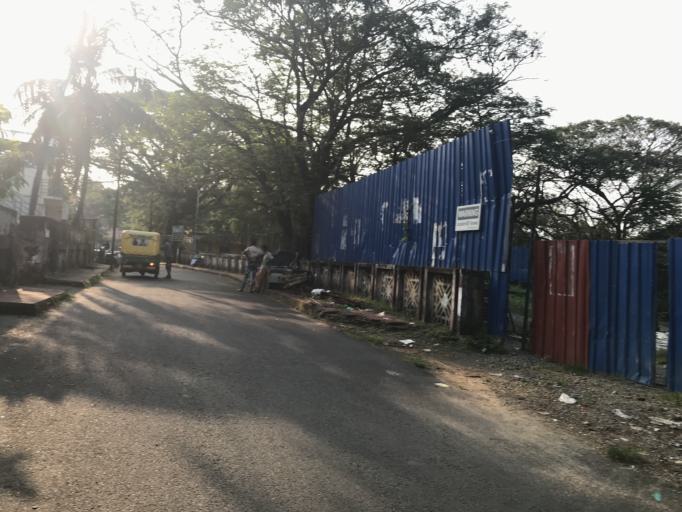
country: IN
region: Kerala
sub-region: Ernakulam
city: Cochin
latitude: 9.9651
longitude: 76.2471
